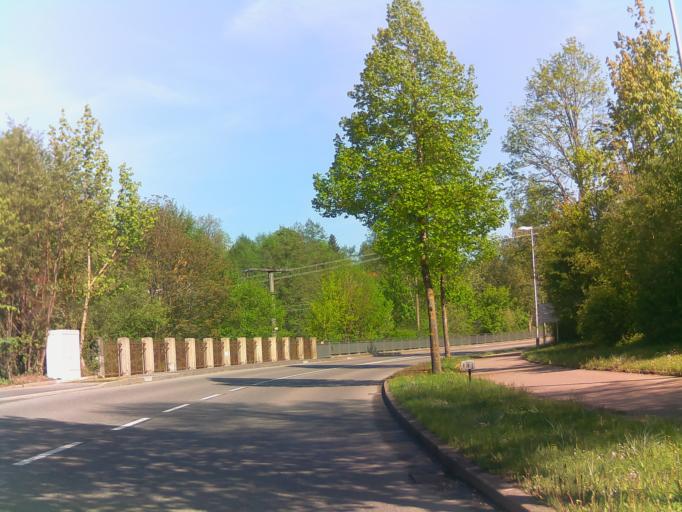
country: DE
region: Baden-Wuerttemberg
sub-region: Karlsruhe Region
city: Ebhausen
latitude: 48.5816
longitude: 8.6768
